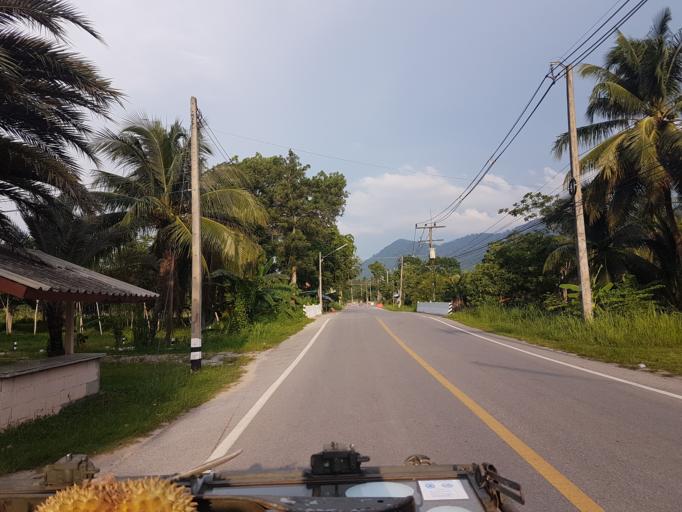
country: TH
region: Pattani
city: Khok Pho
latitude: 6.6761
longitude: 101.0951
